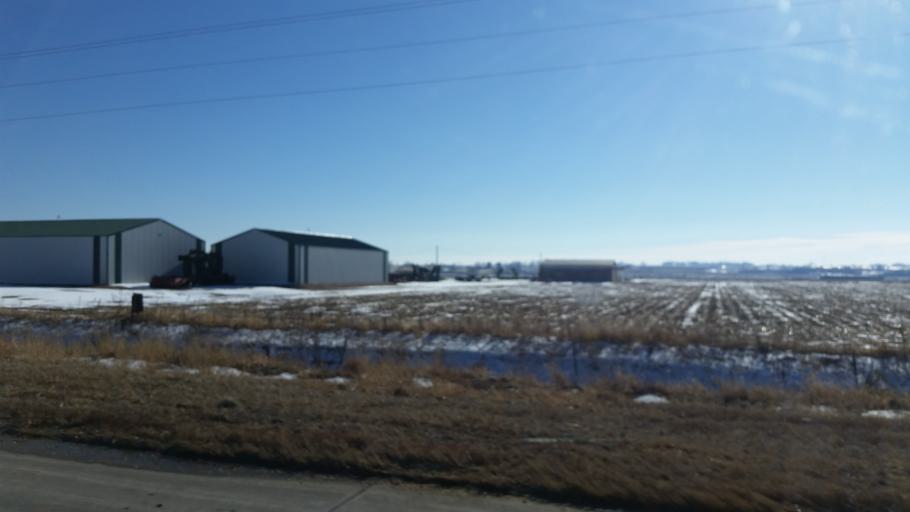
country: US
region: Colorado
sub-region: Weld County
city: Kersey
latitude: 40.3919
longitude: -104.5884
